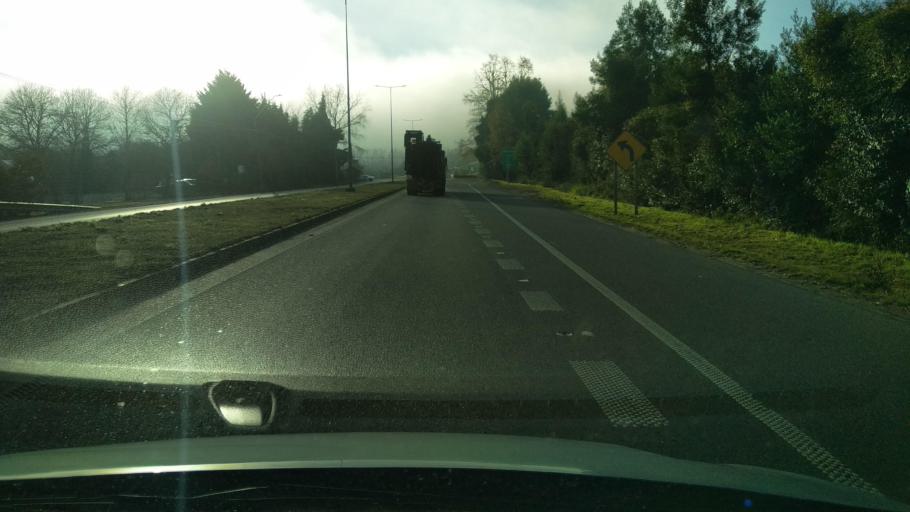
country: CL
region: Los Lagos
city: Las Animas
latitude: -39.7741
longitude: -73.2188
